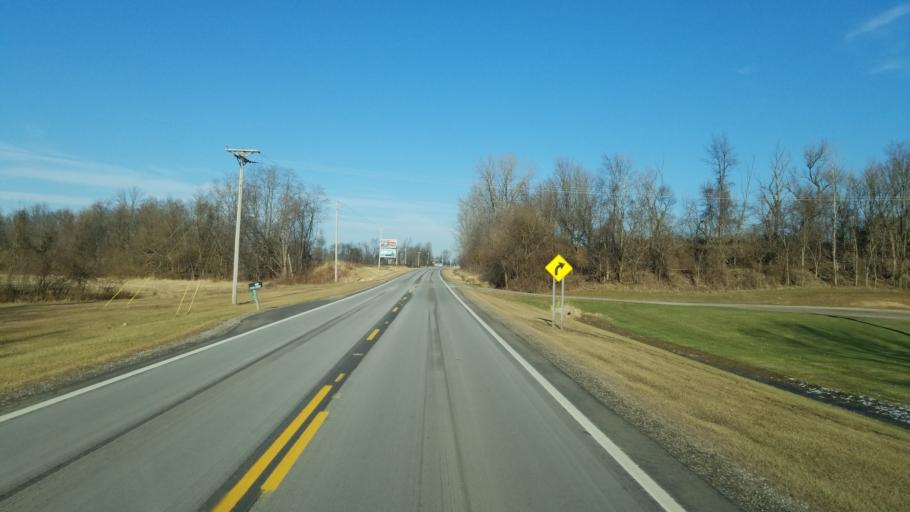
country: US
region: Ohio
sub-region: Huron County
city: Norwalk
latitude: 41.1698
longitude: -82.6454
